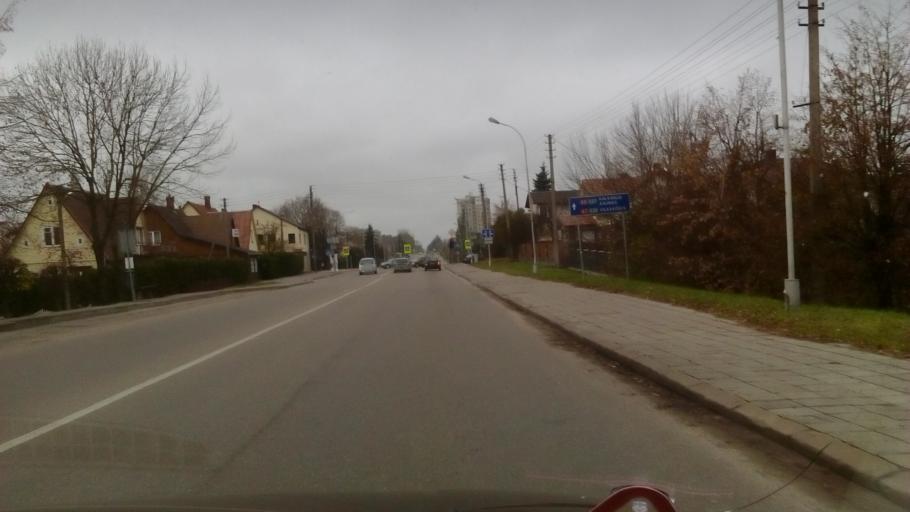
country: LT
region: Marijampoles apskritis
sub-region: Marijampole Municipality
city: Marijampole
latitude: 54.5597
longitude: 23.3439
